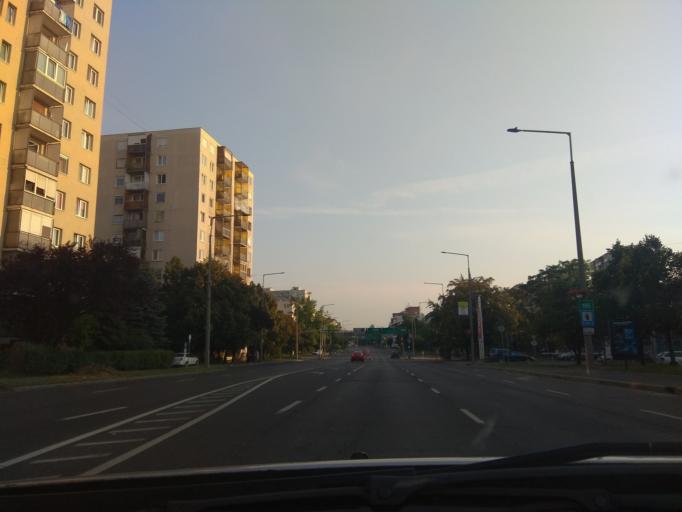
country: HU
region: Borsod-Abauj-Zemplen
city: Miskolc
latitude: 48.0987
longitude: 20.7924
